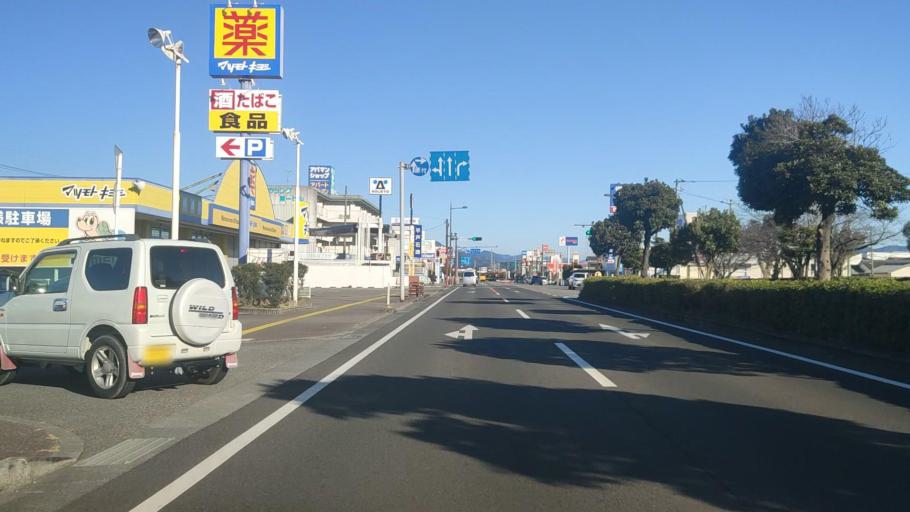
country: JP
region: Miyazaki
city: Nobeoka
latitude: 32.5731
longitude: 131.6836
